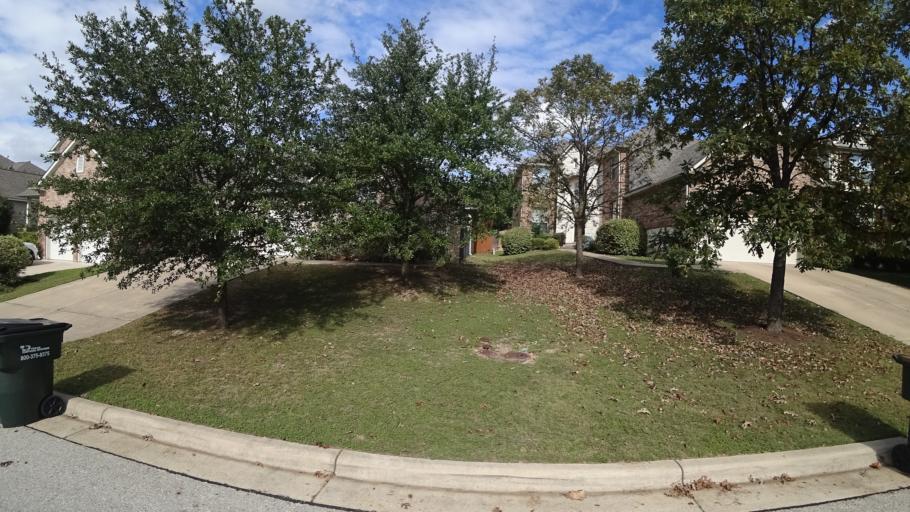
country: US
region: Texas
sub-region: Travis County
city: Hudson Bend
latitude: 30.3622
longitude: -97.9025
